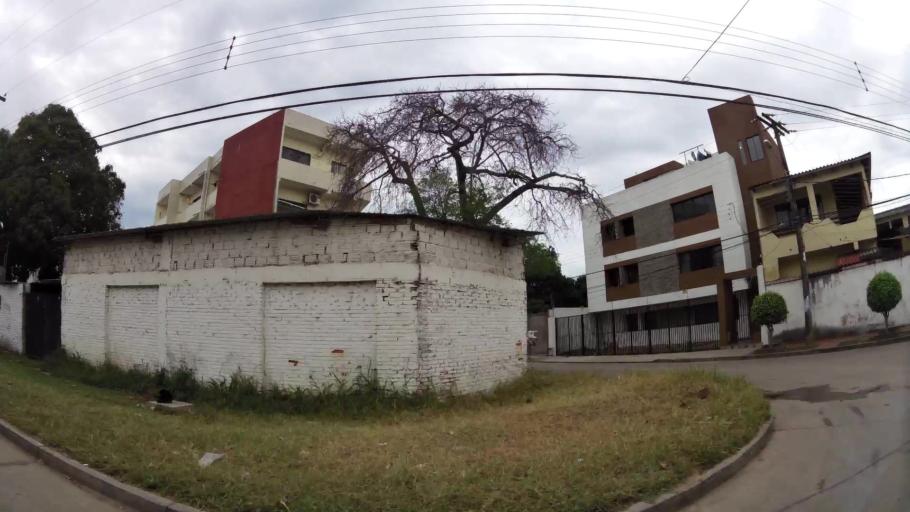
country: BO
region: Santa Cruz
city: Santa Cruz de la Sierra
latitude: -17.7752
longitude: -63.2043
